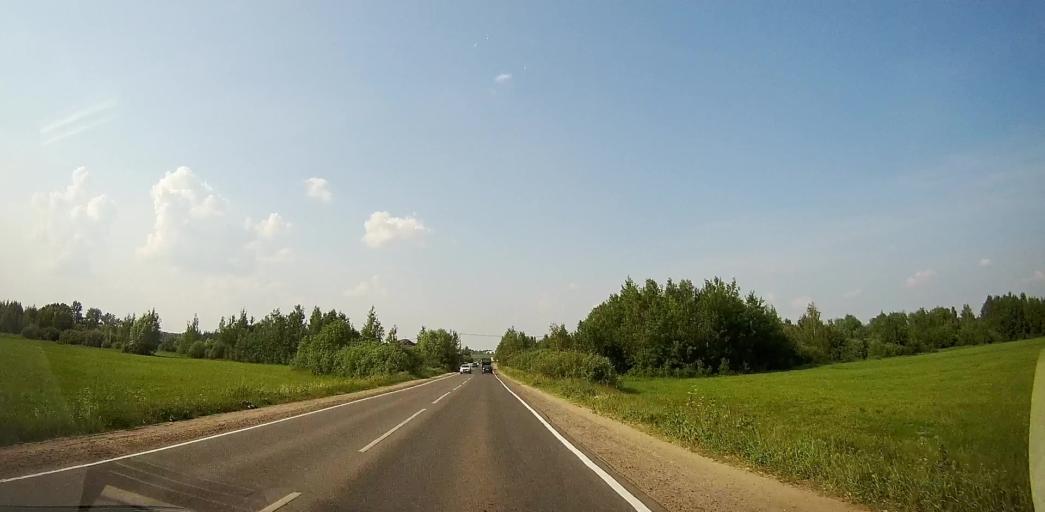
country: RU
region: Moskovskaya
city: Zhitnevo
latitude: 55.3219
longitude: 37.8999
